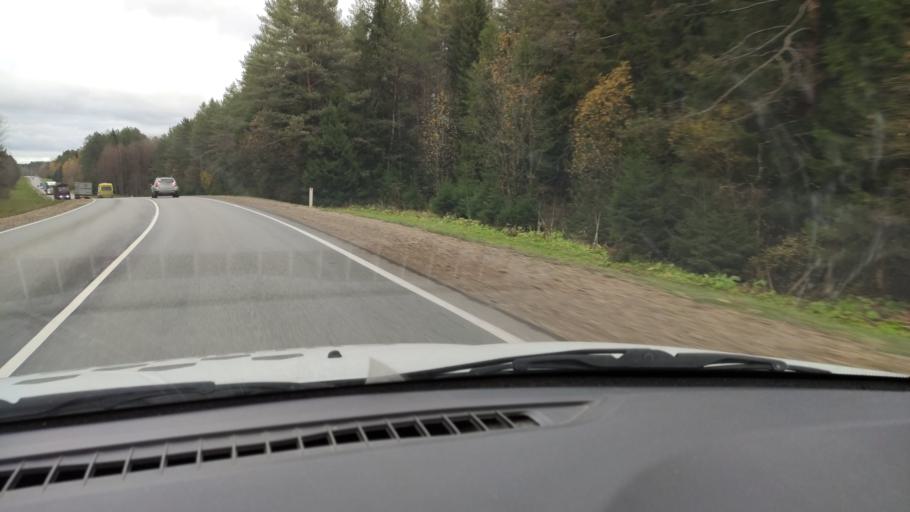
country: RU
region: Kirov
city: Slobodskoy
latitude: 58.7674
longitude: 50.3631
